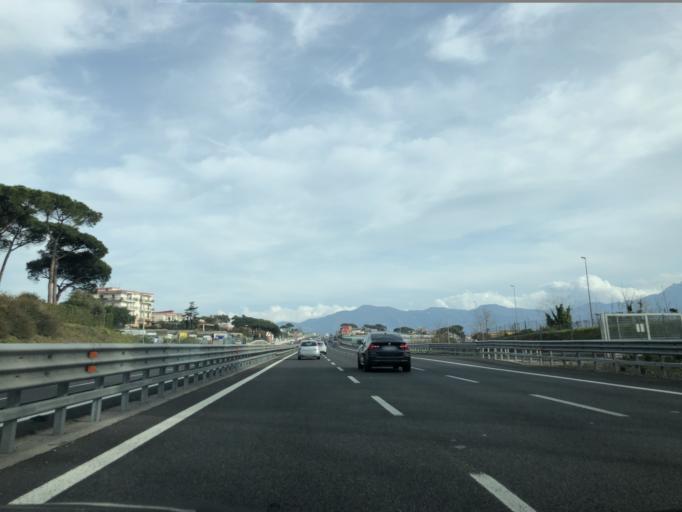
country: IT
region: Campania
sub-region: Provincia di Napoli
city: Torre del Greco
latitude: 40.7753
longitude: 14.4056
